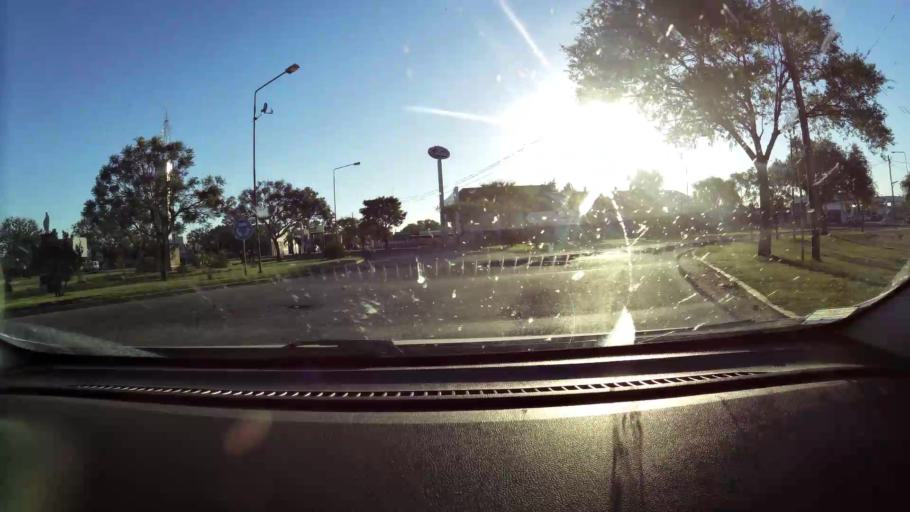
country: AR
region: Cordoba
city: Las Varillas
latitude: -31.8687
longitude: -62.7079
